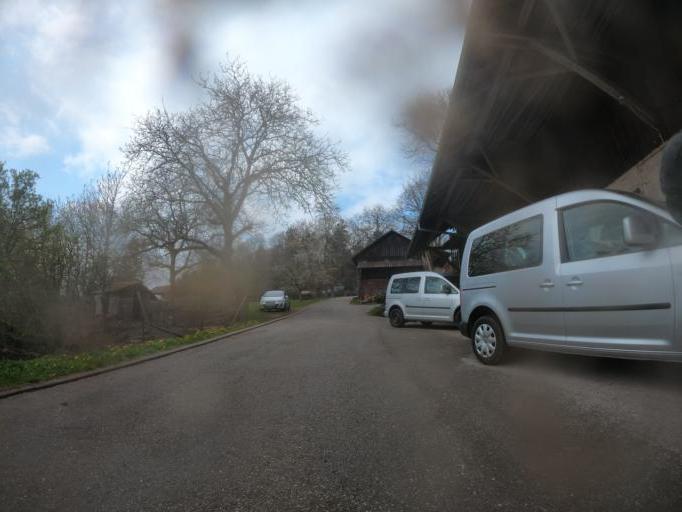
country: DE
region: Baden-Wuerttemberg
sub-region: Karlsruhe Region
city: Neuweiler
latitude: 48.6908
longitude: 8.5827
